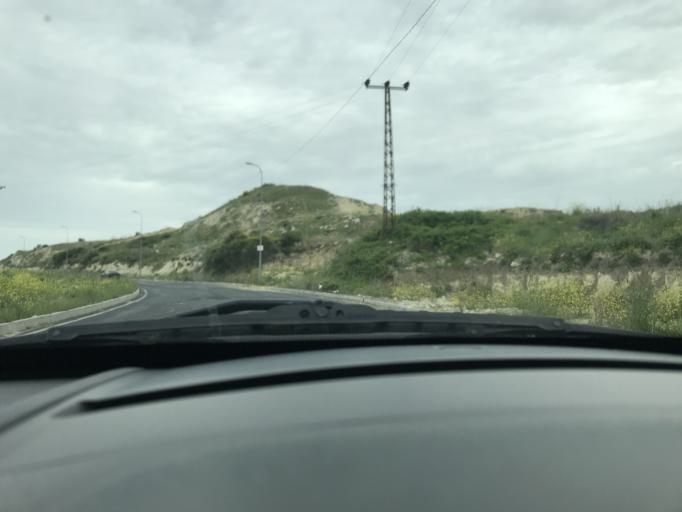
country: TR
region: Istanbul
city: Esenyurt
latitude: 41.0941
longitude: 28.6800
